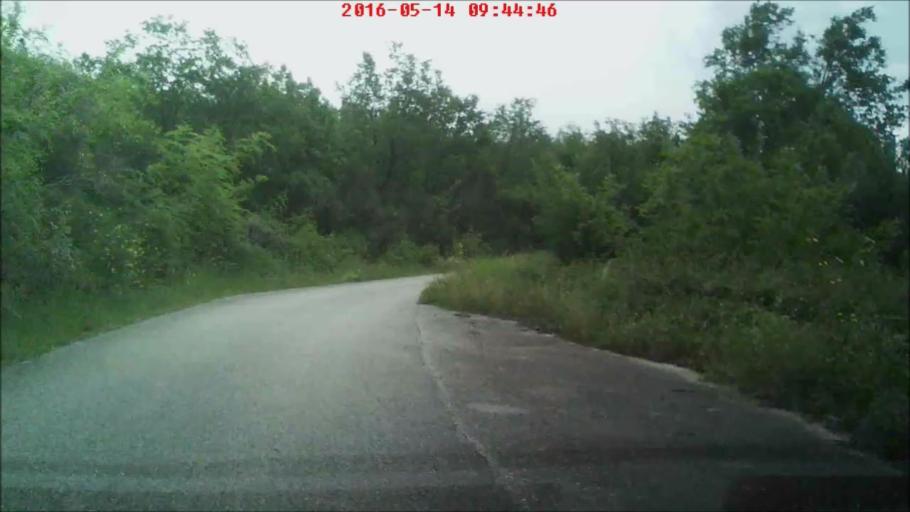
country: HR
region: Dubrovacko-Neretvanska
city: Podgora
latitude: 42.7837
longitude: 17.9103
